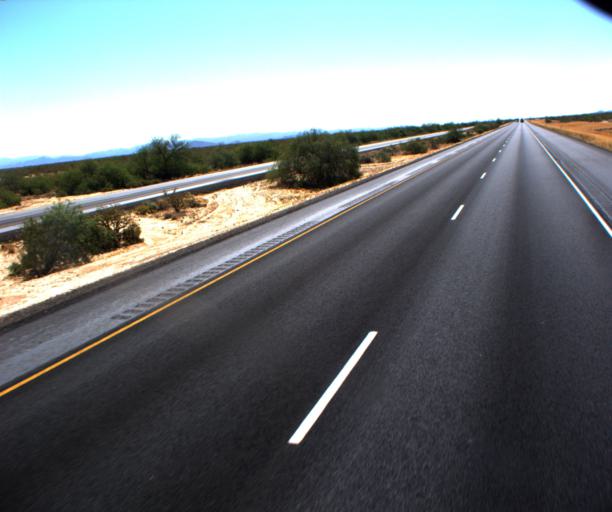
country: US
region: Arizona
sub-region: Yavapai County
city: Congress
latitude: 34.0866
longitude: -112.8982
